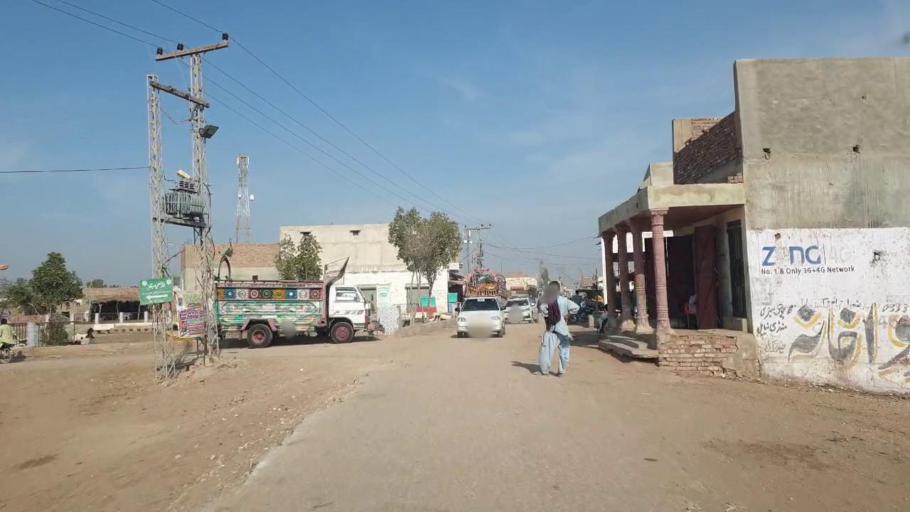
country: PK
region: Sindh
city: Sann
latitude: 25.9064
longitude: 68.2341
